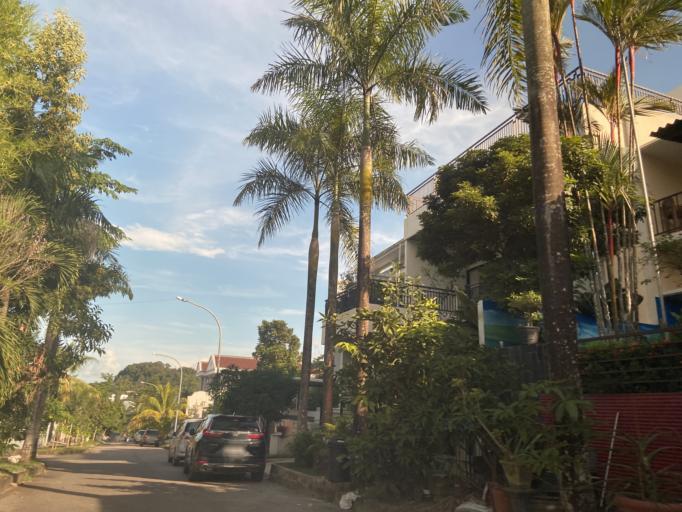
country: SG
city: Singapore
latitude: 1.1069
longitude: 104.0232
